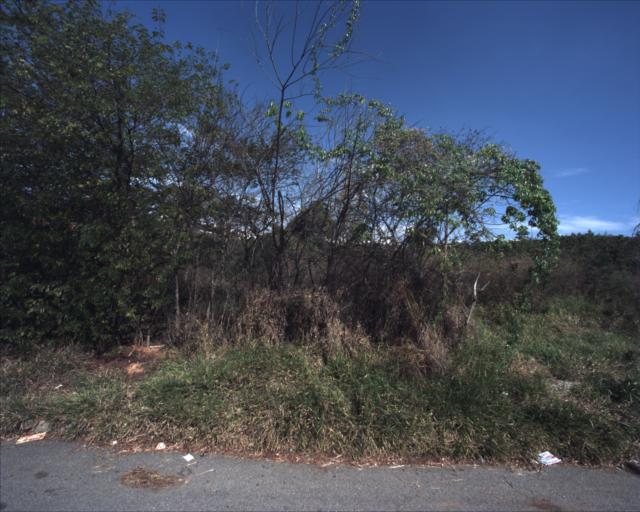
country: BR
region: Sao Paulo
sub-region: Sorocaba
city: Sorocaba
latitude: -23.4836
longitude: -47.5081
